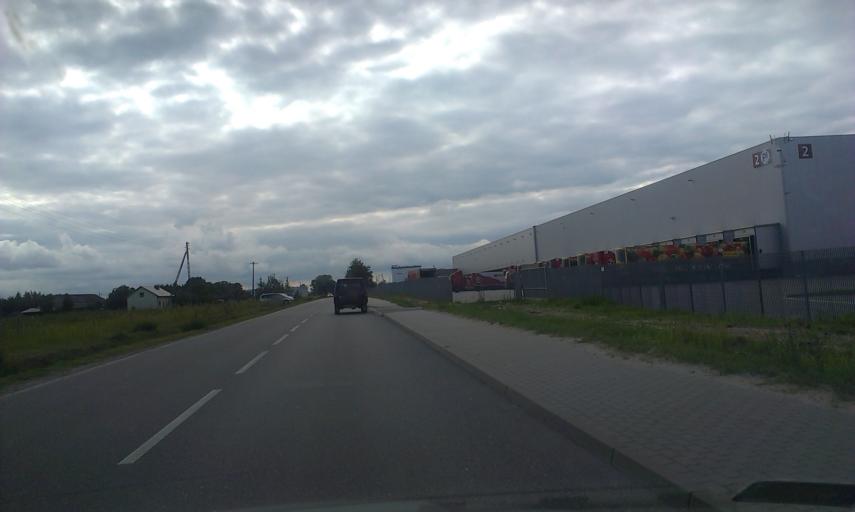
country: PL
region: Masovian Voivodeship
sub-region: Powiat zyrardowski
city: Radziejowice
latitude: 51.9726
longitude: 20.5634
